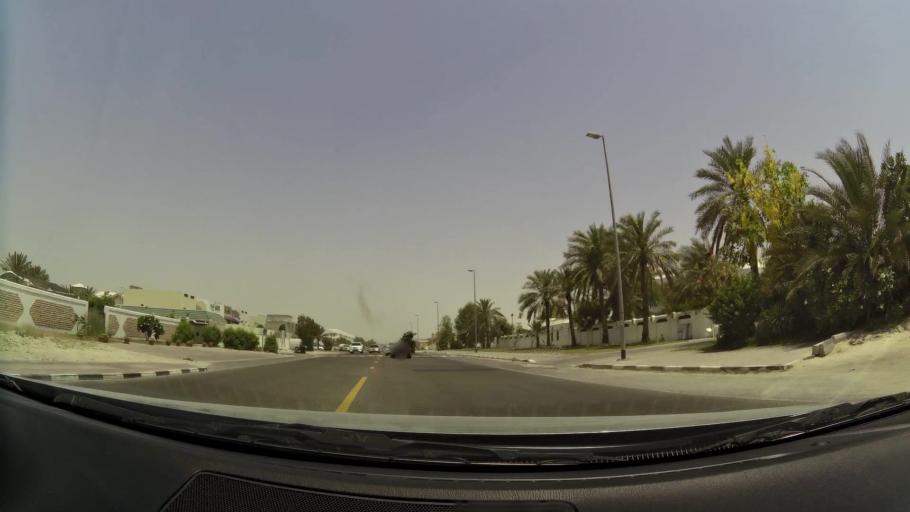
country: AE
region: Dubai
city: Dubai
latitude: 25.1441
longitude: 55.1987
